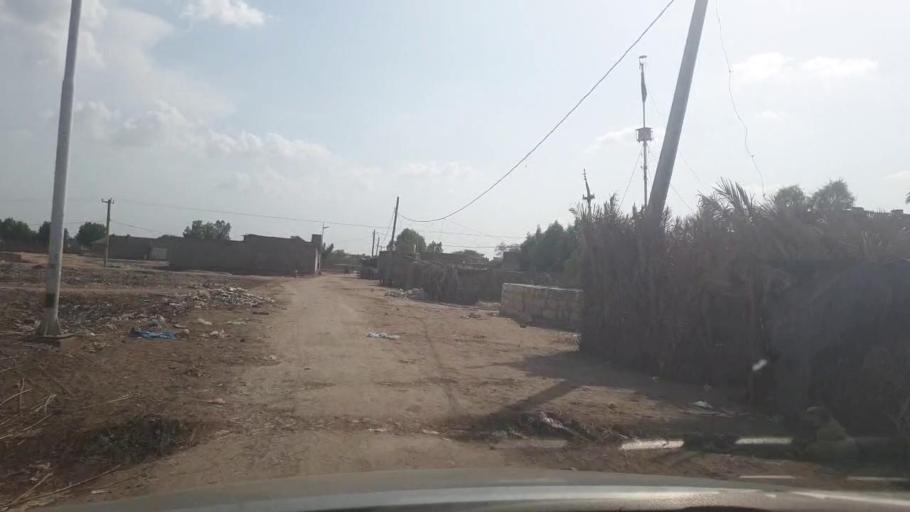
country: PK
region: Sindh
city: Khairpur
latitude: 27.5284
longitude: 68.7720
